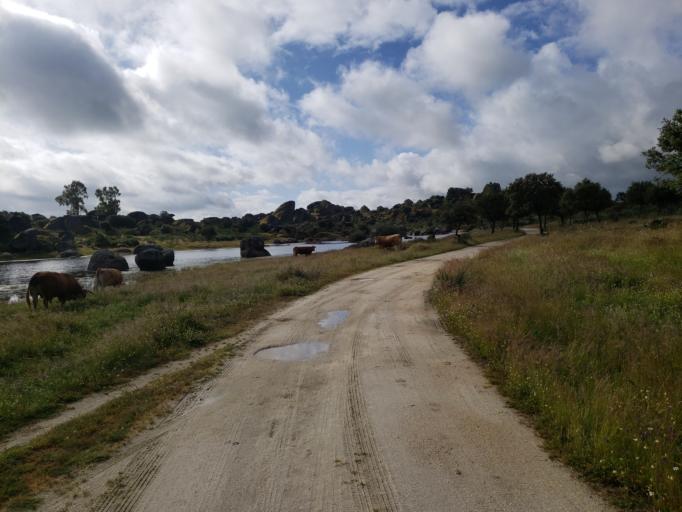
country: ES
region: Extremadura
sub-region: Provincia de Caceres
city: Malpartida de Caceres
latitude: 39.4261
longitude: -6.4995
